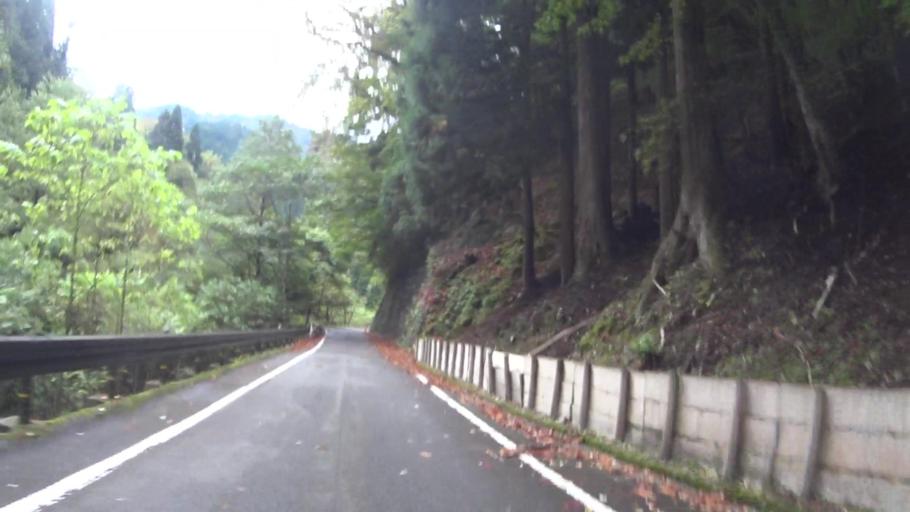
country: JP
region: Fukui
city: Obama
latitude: 35.2782
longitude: 135.7191
